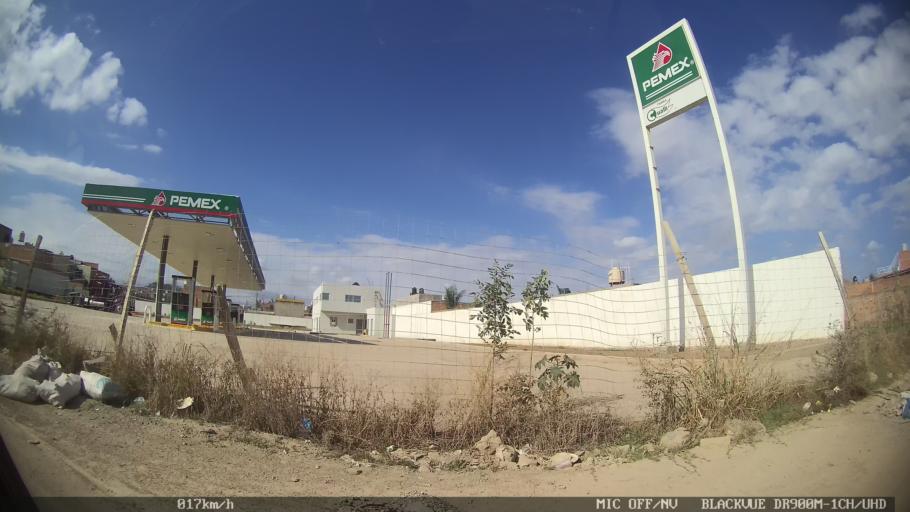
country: MX
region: Jalisco
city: Tonala
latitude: 20.6546
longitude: -103.2436
